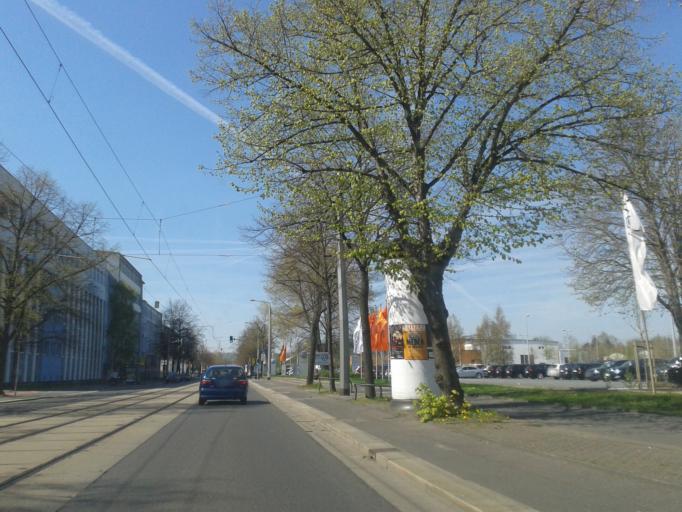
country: DE
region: Saxony
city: Dresden
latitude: 51.0589
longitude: 13.7047
